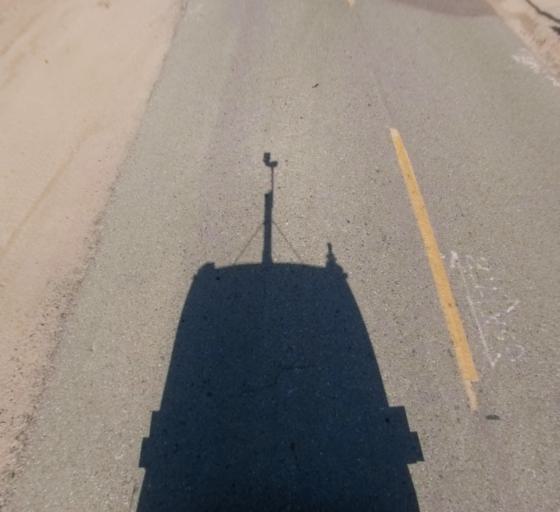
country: US
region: California
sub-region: Fresno County
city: Biola
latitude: 36.8296
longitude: -120.0696
